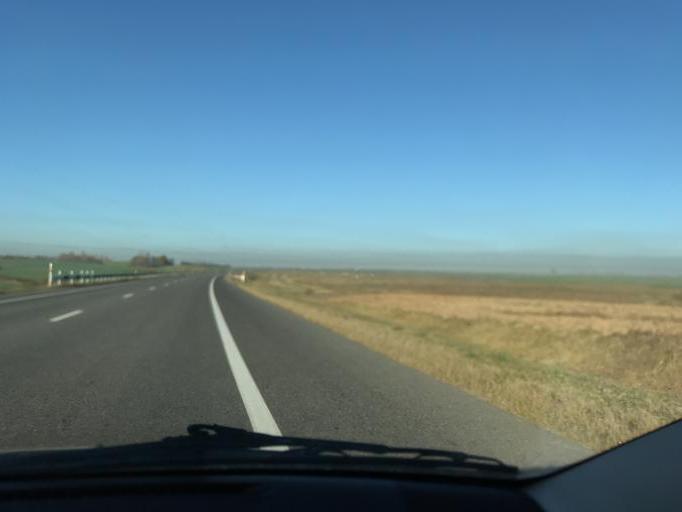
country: BY
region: Vitebsk
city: Vitebsk
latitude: 55.1019
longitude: 30.1309
